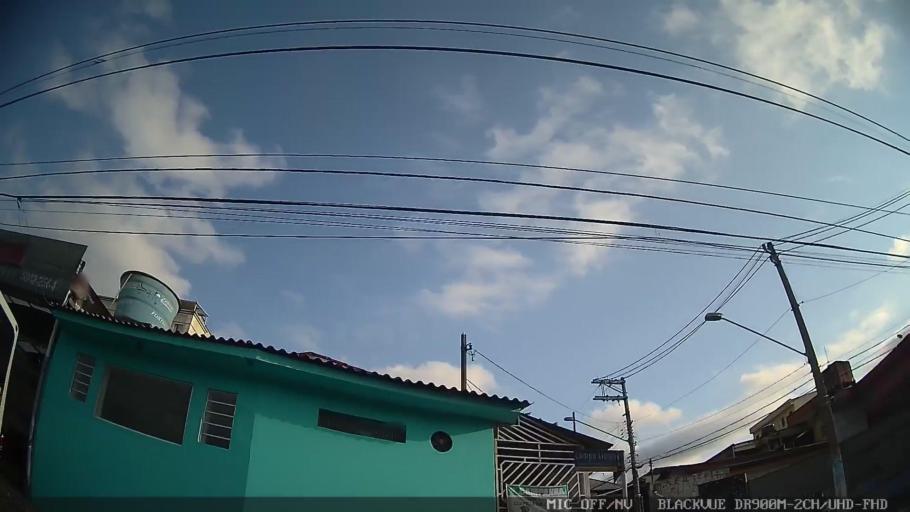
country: BR
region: Sao Paulo
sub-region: Taboao Da Serra
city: Taboao da Serra
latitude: -23.6222
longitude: -46.7589
